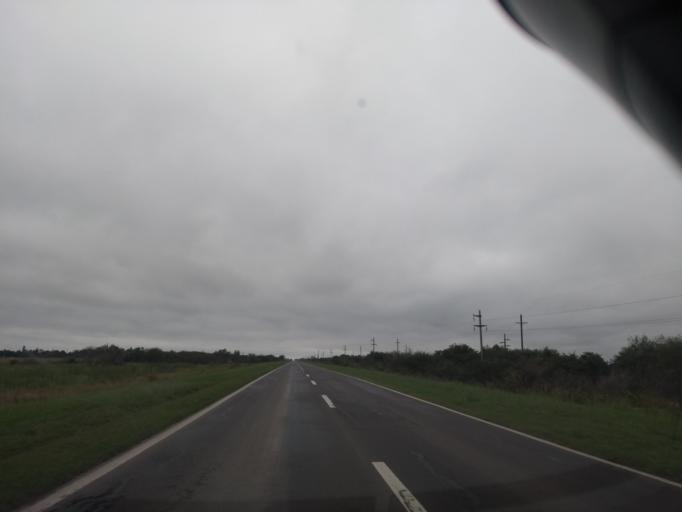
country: AR
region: Chaco
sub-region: Departamento de Quitilipi
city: Quitilipi
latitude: -26.8599
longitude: -60.2848
